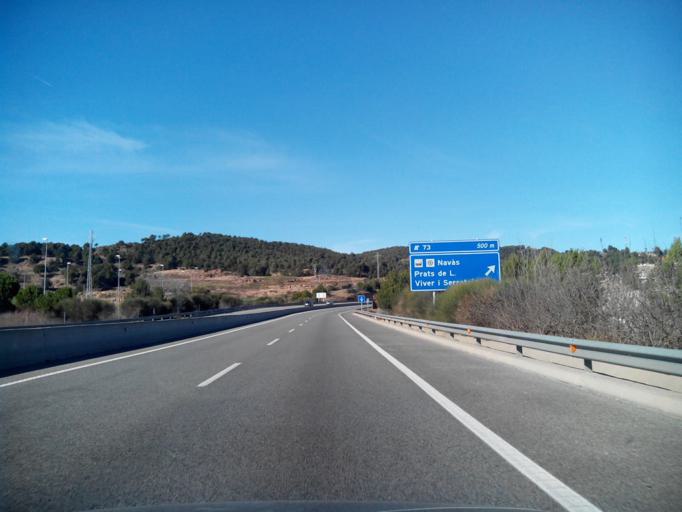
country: ES
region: Catalonia
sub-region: Provincia de Barcelona
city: Navas
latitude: 41.8962
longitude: 1.8705
